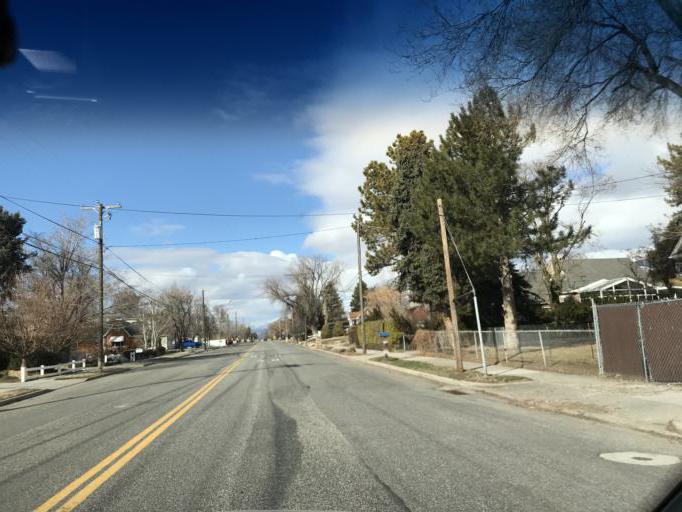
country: US
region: Utah
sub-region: Davis County
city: Woods Cross
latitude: 40.8666
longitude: -111.9020
